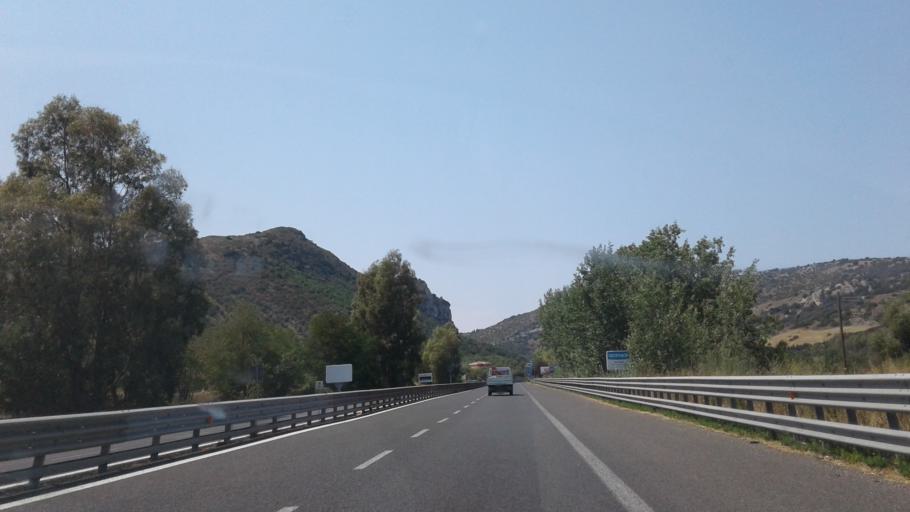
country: IT
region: Sardinia
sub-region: Provincia di Sassari
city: Muros
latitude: 40.6908
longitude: 8.6237
